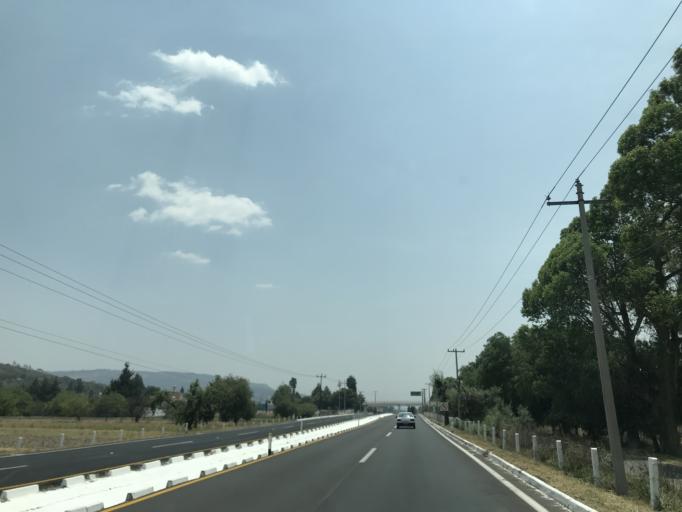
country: MX
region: Tlaxcala
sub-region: Ixtacuixtla de Mariano Matamoros
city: Santa Justina Ecatepec
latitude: 19.3277
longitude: -98.3374
